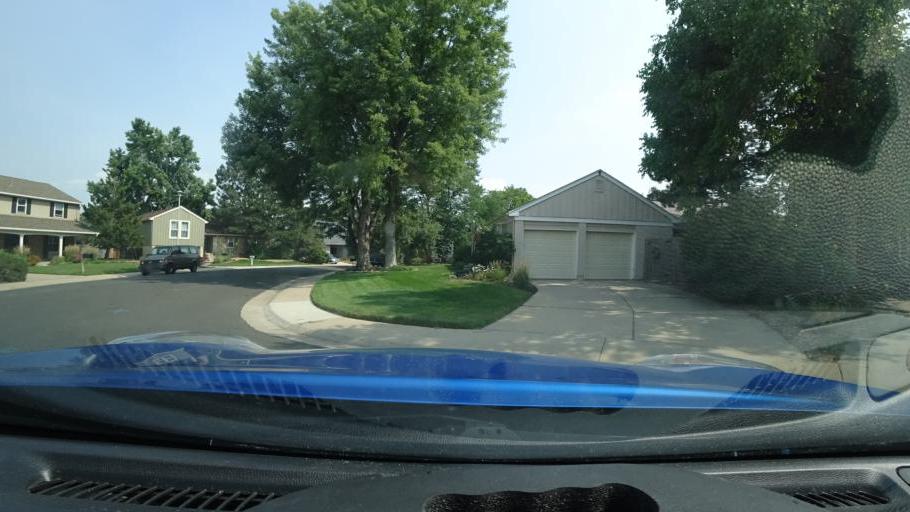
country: US
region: Colorado
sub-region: Adams County
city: Aurora
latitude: 39.6670
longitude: -104.8484
